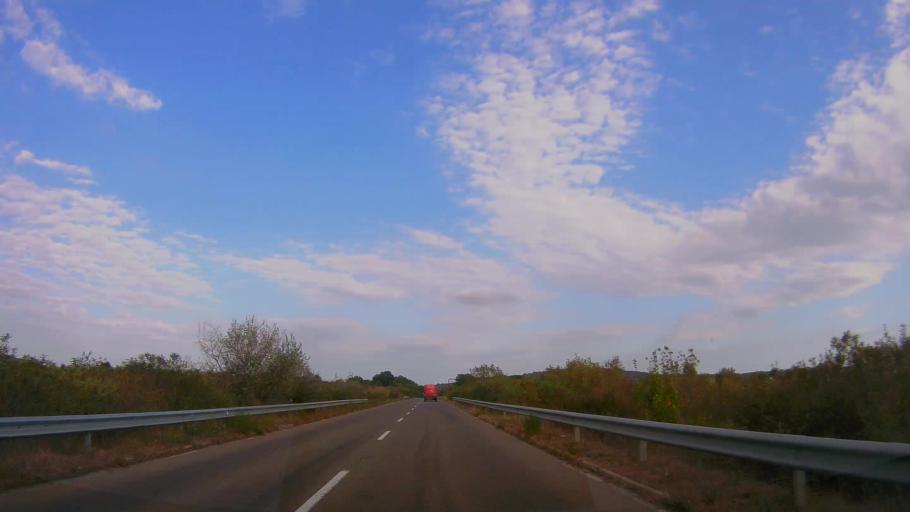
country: BG
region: Burgas
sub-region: Obshtina Sozopol
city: Sozopol
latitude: 42.3548
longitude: 27.7065
